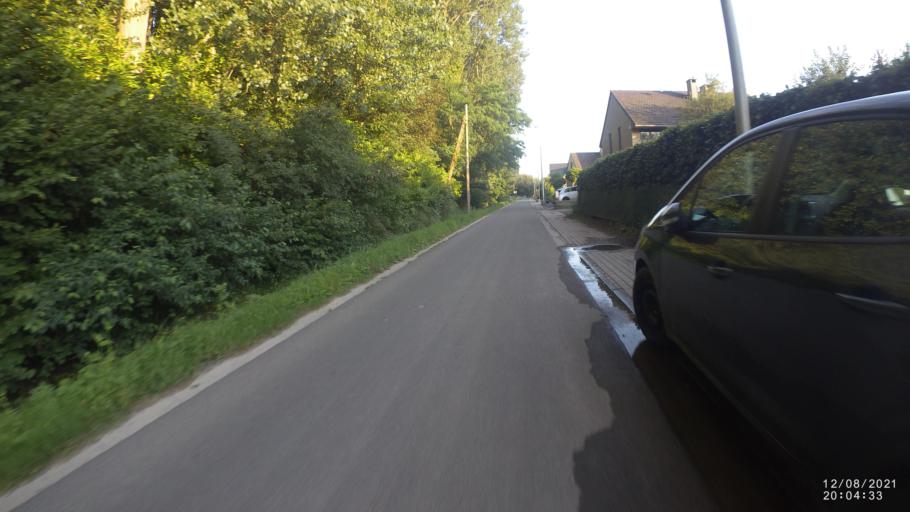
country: BE
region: Flanders
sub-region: Provincie Vlaams-Brabant
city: Dilbeek
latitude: 50.8593
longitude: 4.2142
